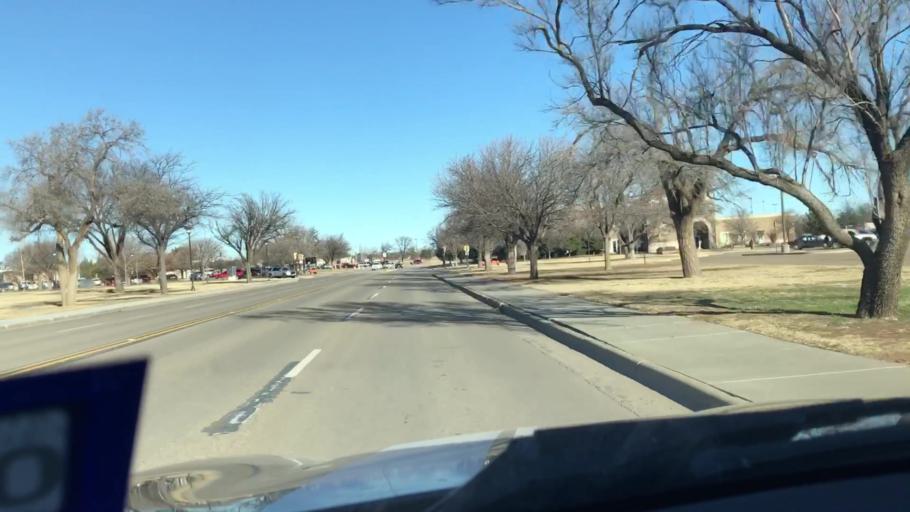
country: US
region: Texas
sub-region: Lubbock County
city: Lubbock
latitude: 33.5844
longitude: -101.8819
